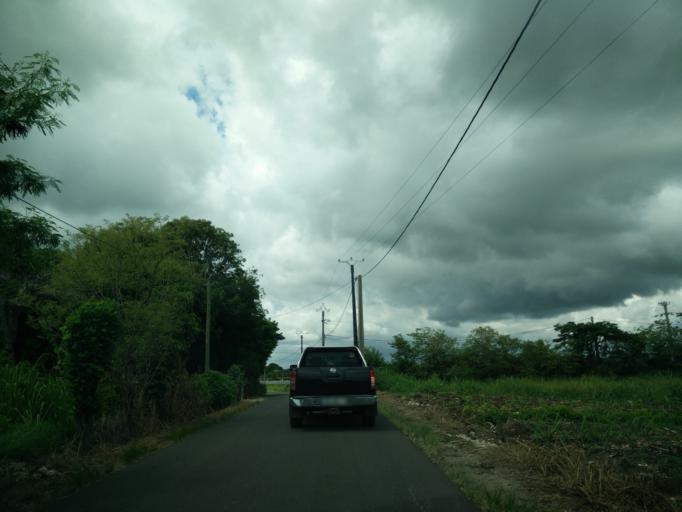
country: GP
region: Guadeloupe
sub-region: Guadeloupe
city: Le Moule
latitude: 16.2983
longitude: -61.3440
